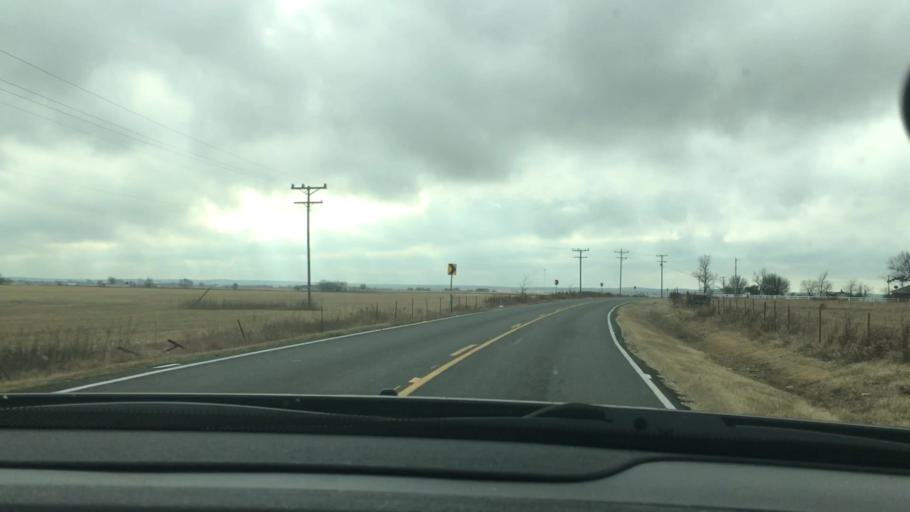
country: US
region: Oklahoma
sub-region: Bryan County
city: Durant
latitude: 34.1216
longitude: -96.4881
